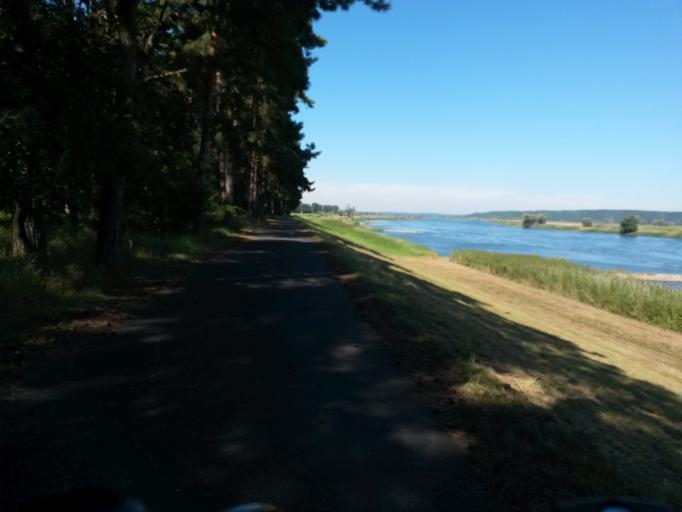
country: PL
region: West Pomeranian Voivodeship
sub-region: Powiat gryfinski
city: Cedynia
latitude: 52.8943
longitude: 14.1544
